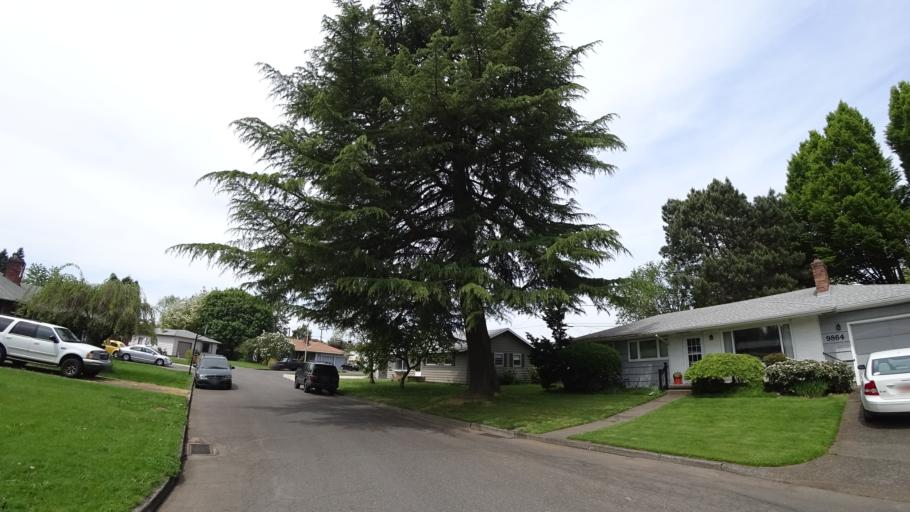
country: US
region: Oregon
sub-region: Clackamas County
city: Milwaukie
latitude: 45.4513
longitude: -122.6137
